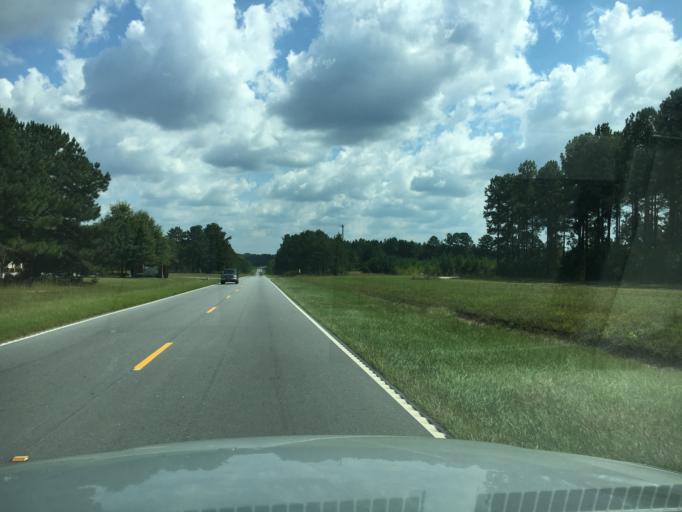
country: US
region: South Carolina
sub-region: Greenwood County
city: Greenwood
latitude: 34.1557
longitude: -82.1702
